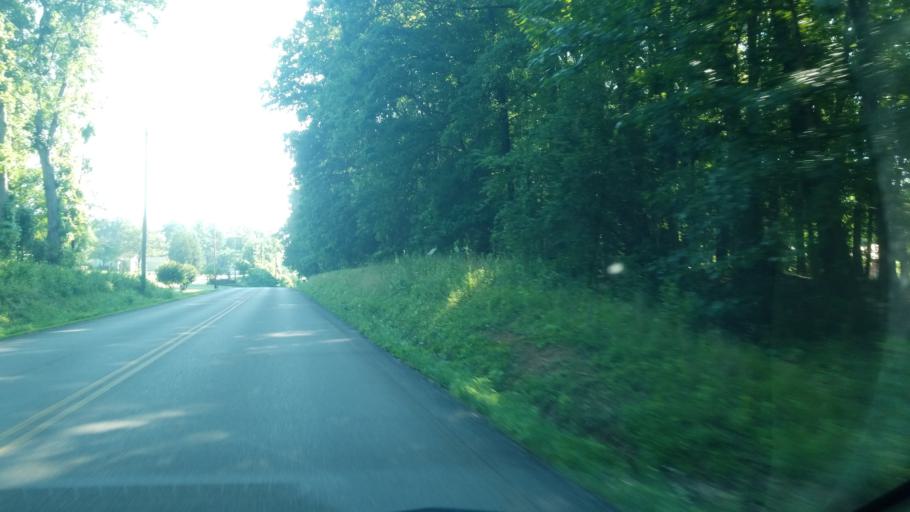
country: US
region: Tennessee
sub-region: Loudon County
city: Loudon
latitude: 35.8076
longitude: -84.3490
